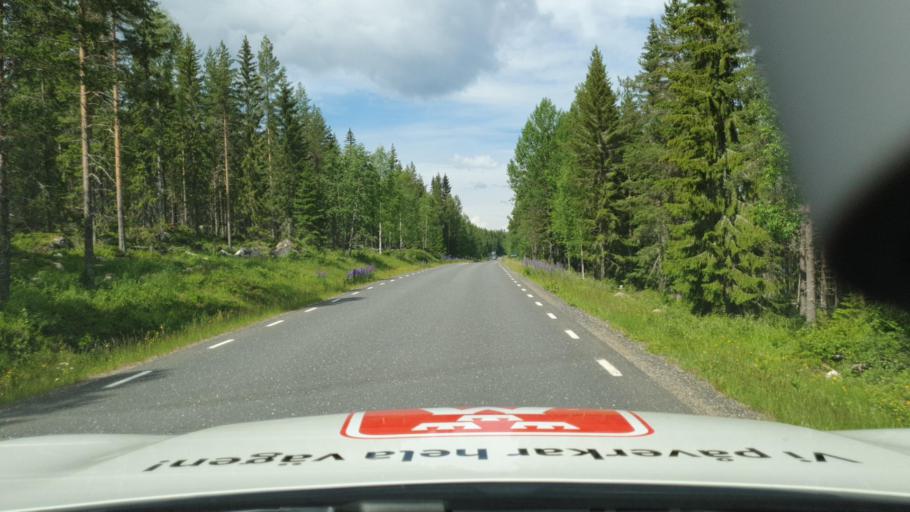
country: SE
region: Vaermland
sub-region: Torsby Kommun
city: Torsby
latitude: 60.6422
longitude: 12.6949
